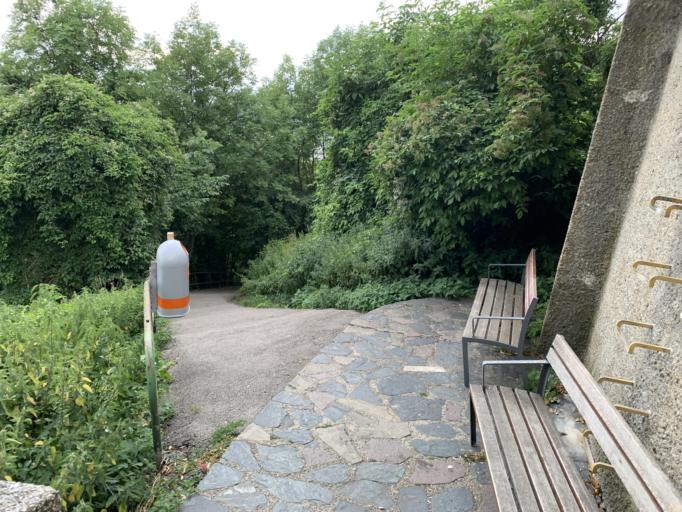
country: AT
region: Lower Austria
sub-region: Politischer Bezirk Korneuburg
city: Langenzersdorf
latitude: 48.2781
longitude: 16.3473
